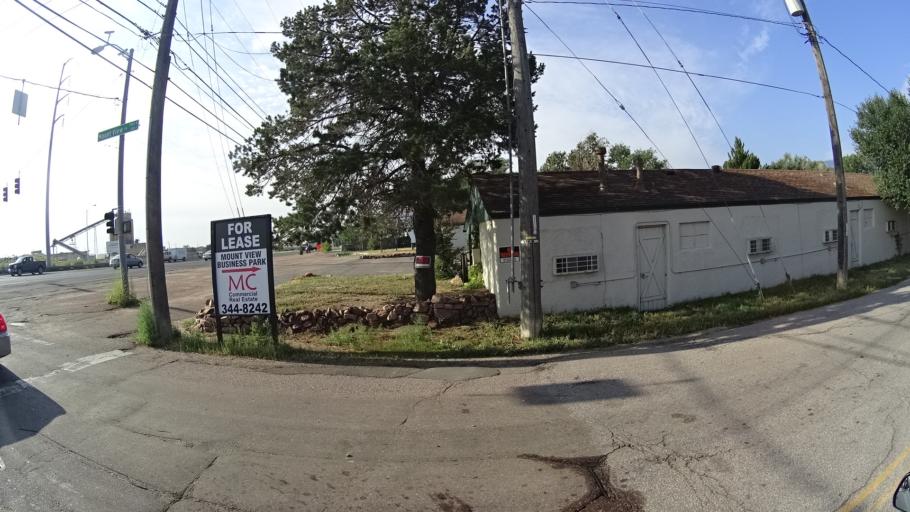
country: US
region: Colorado
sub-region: El Paso County
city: Colorado Springs
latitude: 38.8896
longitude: -104.8200
